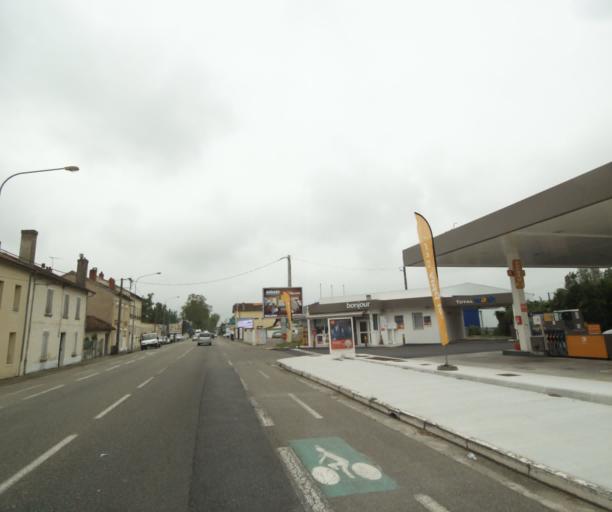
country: FR
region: Midi-Pyrenees
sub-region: Departement du Tarn-et-Garonne
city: Montauban
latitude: 44.0043
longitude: 1.3413
